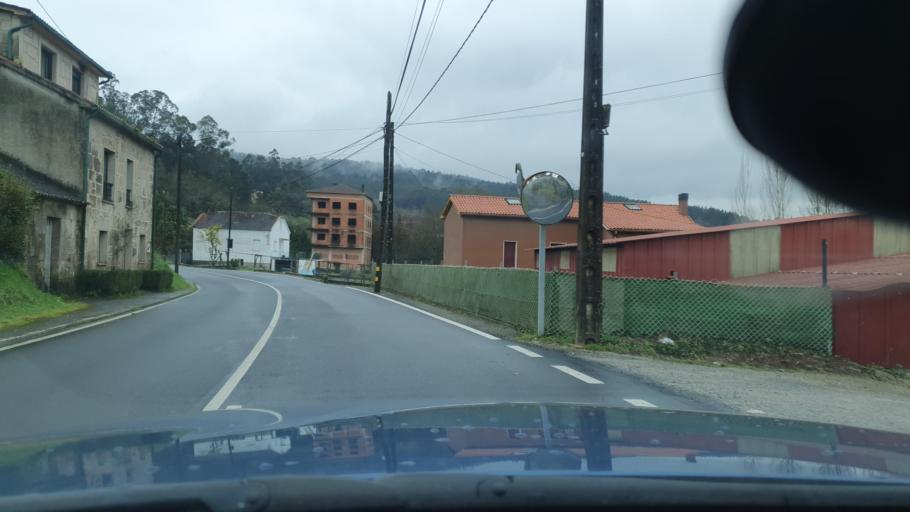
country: ES
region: Galicia
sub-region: Provincia da Coruna
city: Padron
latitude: 42.7500
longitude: -8.6697
